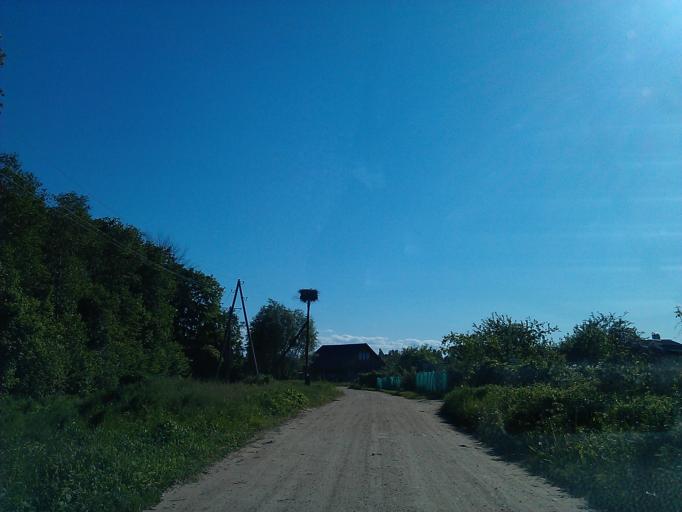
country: LV
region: Adazi
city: Adazi
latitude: 57.0933
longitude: 24.3231
